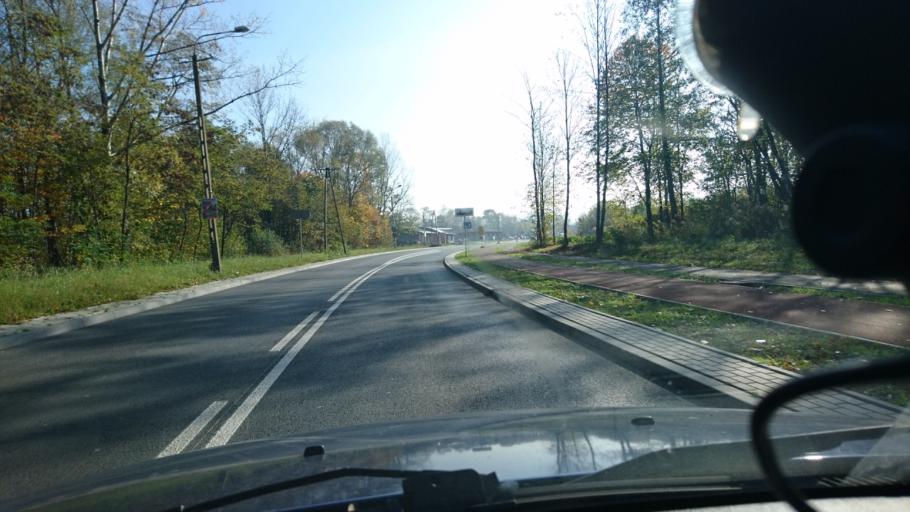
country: PL
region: Silesian Voivodeship
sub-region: Powiat bielski
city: Mazancowice
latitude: 49.8244
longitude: 18.9743
